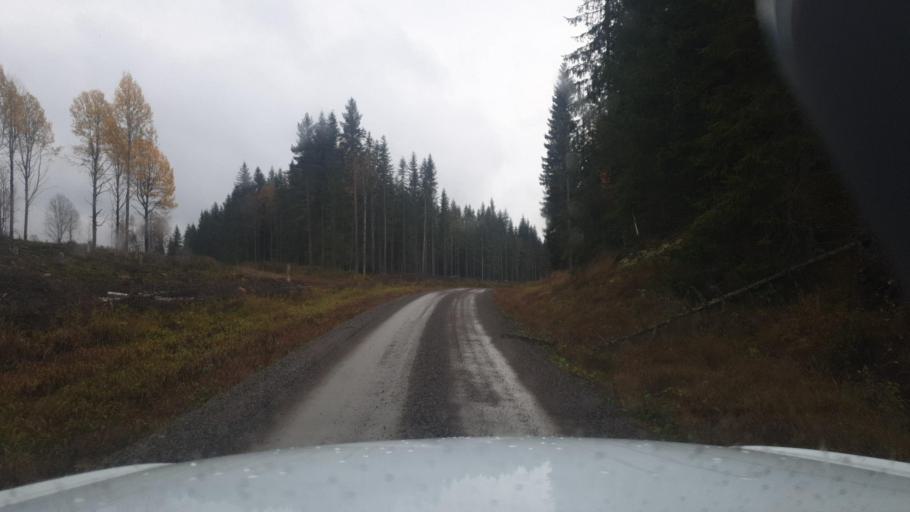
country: SE
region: Vaermland
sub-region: Eda Kommun
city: Charlottenberg
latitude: 60.0511
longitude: 12.6303
